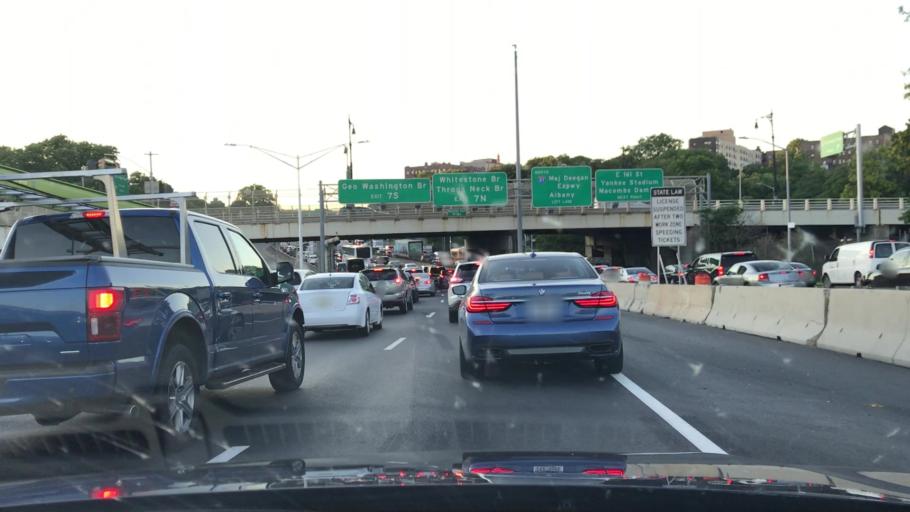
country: US
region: New York
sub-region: New York County
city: Inwood
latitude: 40.8275
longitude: -73.9309
